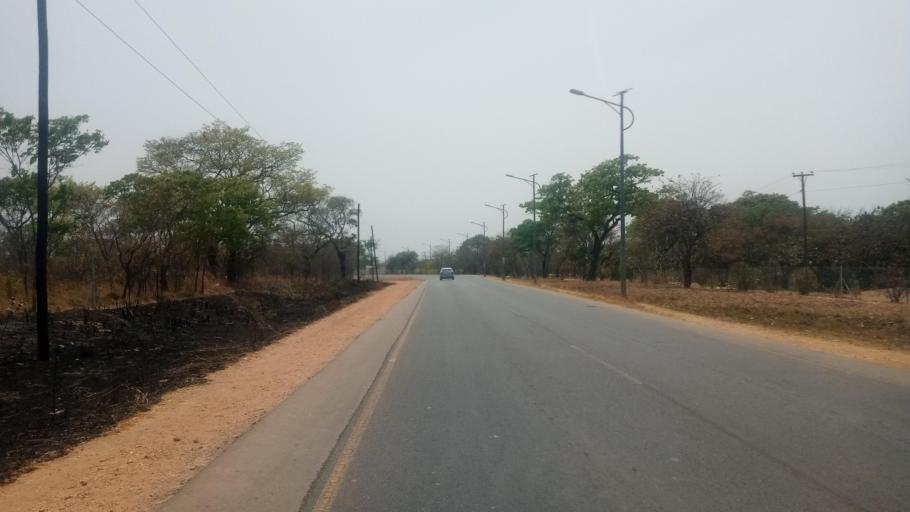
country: ZM
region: Lusaka
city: Lusaka
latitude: -15.4674
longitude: 28.4302
